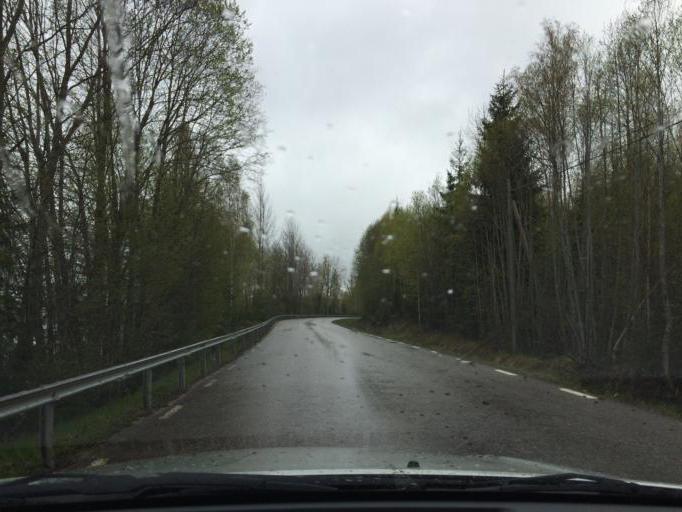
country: SE
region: Dalarna
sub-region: Ludvika Kommun
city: Grangesberg
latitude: 60.0536
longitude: 14.8925
